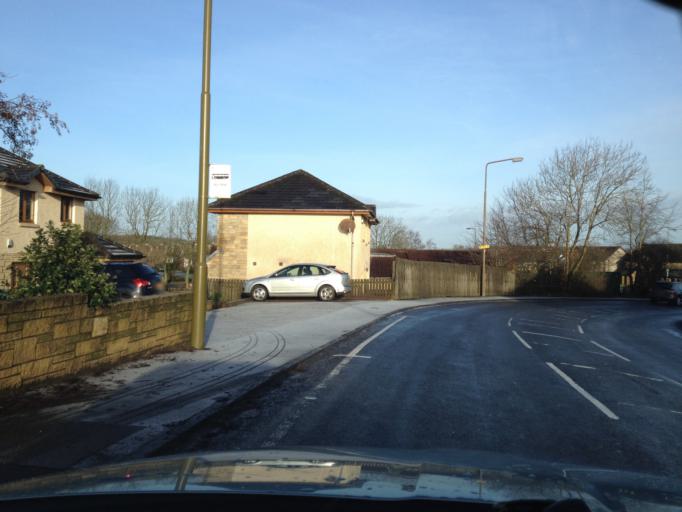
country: GB
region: Scotland
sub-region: West Lothian
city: Bathgate
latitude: 55.8935
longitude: -3.6521
